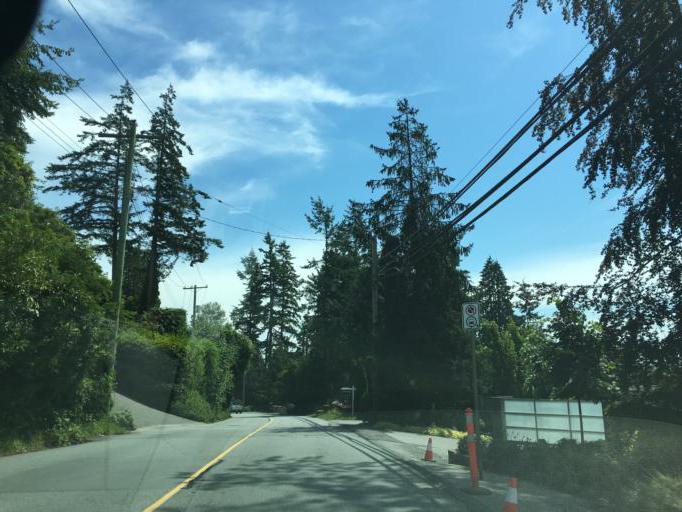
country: CA
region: British Columbia
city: West Vancouver
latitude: 49.3406
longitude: -123.2251
